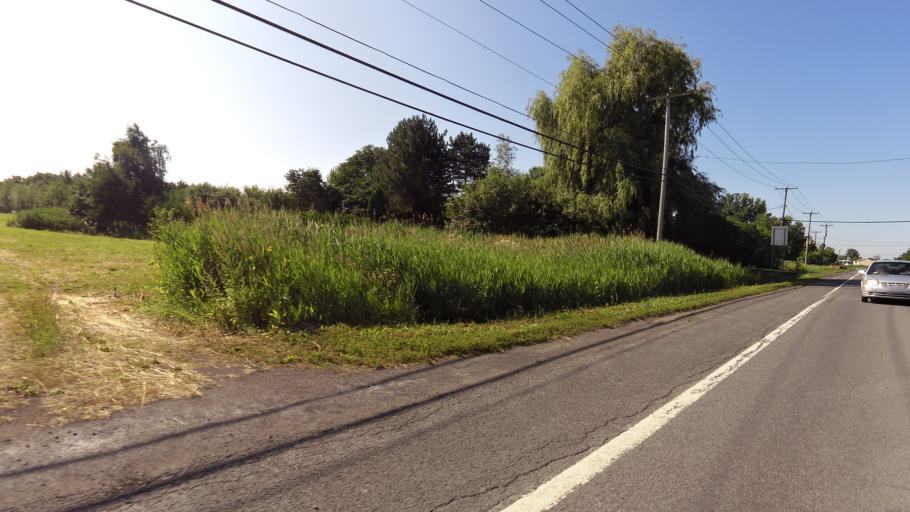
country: CA
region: Quebec
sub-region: Monteregie
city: Saint-Jean-sur-Richelieu
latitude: 45.2982
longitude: -73.3234
